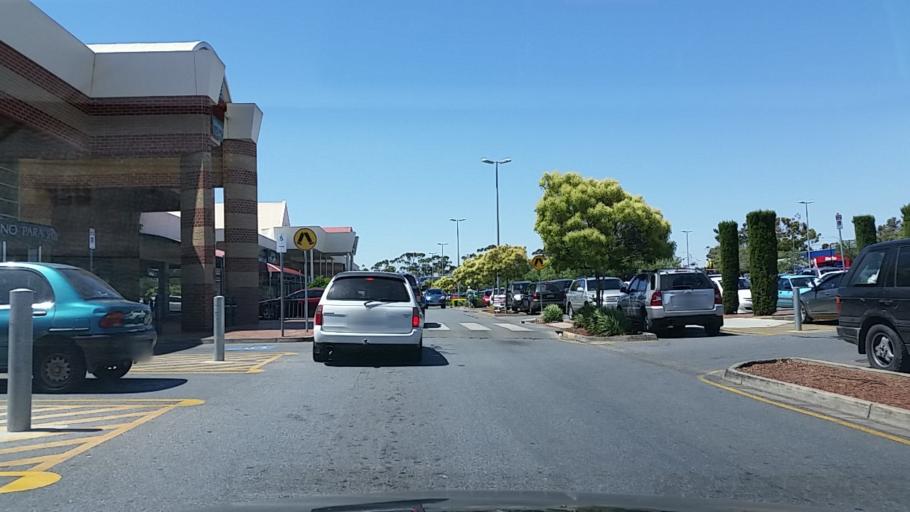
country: AU
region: South Australia
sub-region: Playford
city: Smithfield
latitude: -34.6881
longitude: 138.6890
